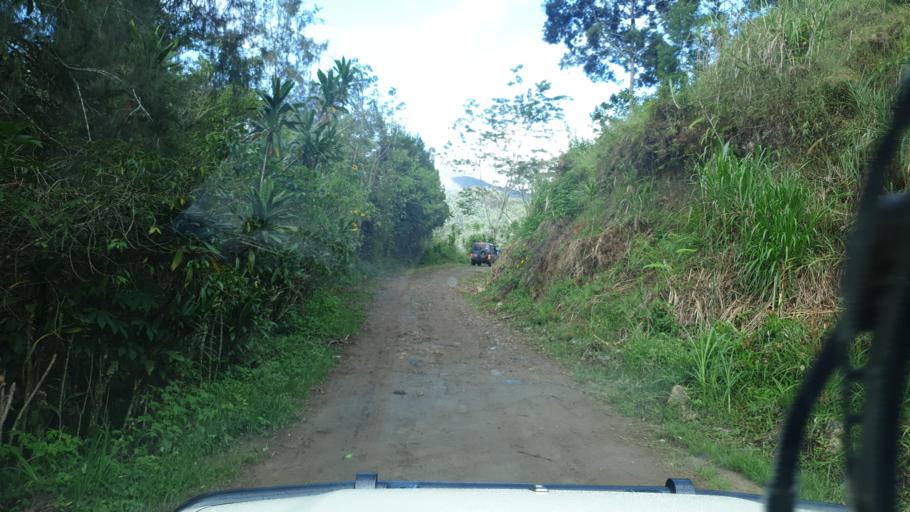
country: PG
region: Eastern Highlands
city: Goroka
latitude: -5.9201
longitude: 145.2568
